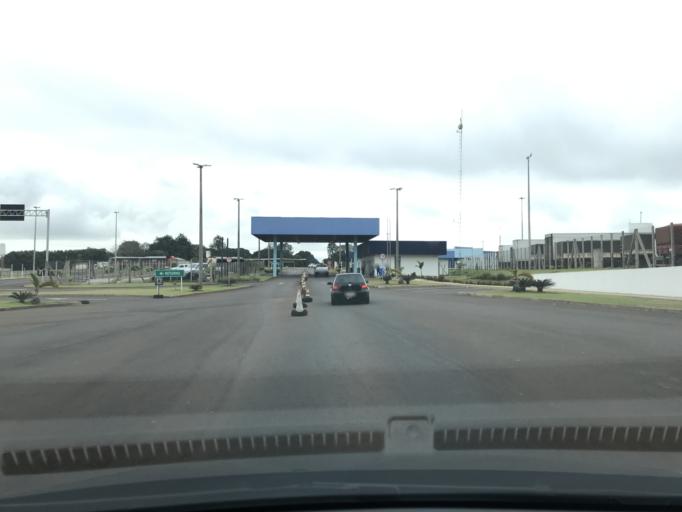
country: PY
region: Canindeyu
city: Salto del Guaira
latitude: -24.0031
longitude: -54.3195
